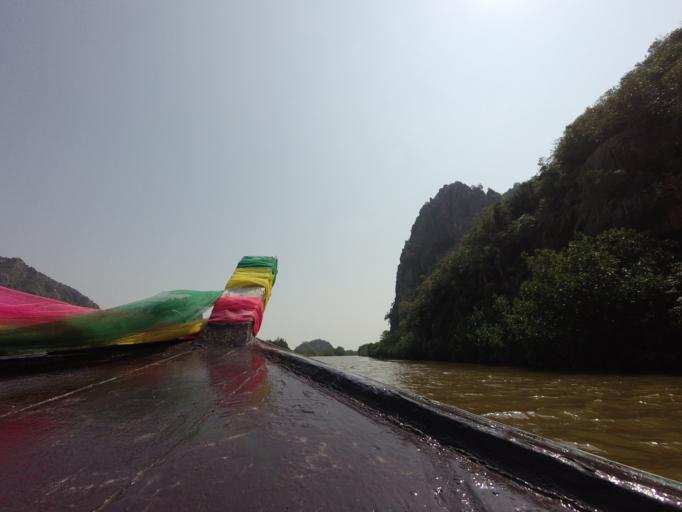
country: TH
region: Prachuap Khiri Khan
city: Kui Buri
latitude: 12.1423
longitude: 99.9538
